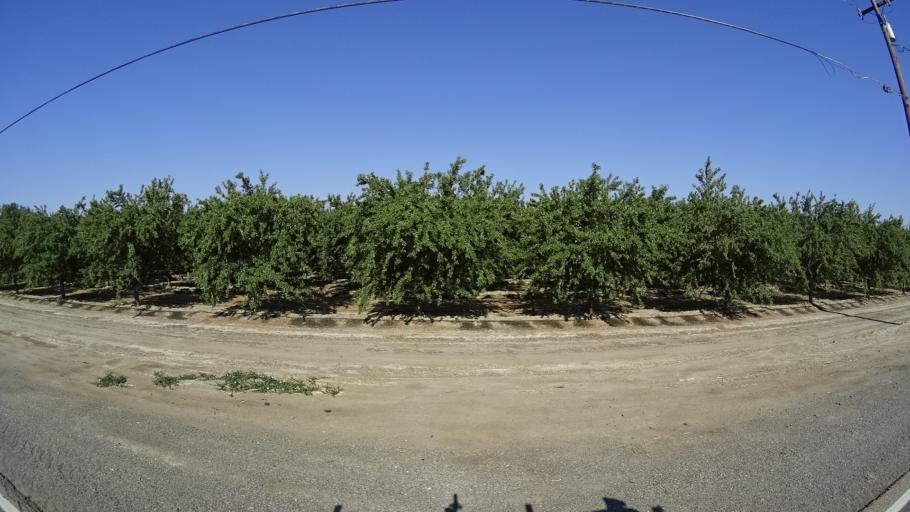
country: US
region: California
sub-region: Kings County
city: Lucerne
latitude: 36.3889
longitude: -119.7090
